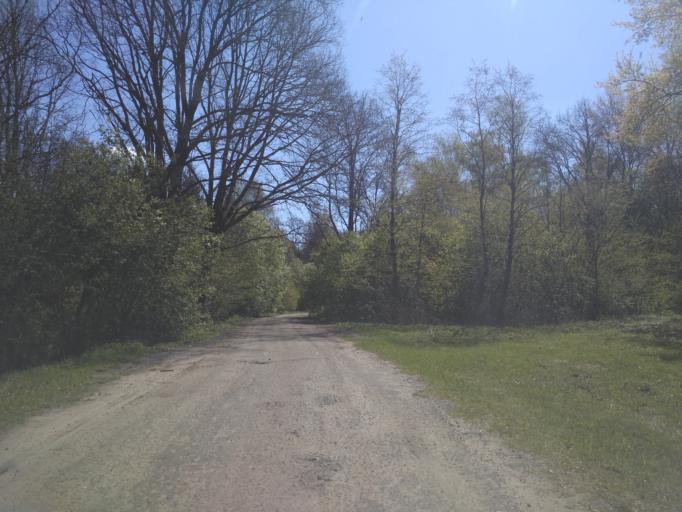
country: BY
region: Mogilev
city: Mstsislaw
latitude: 54.0488
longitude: 31.6958
